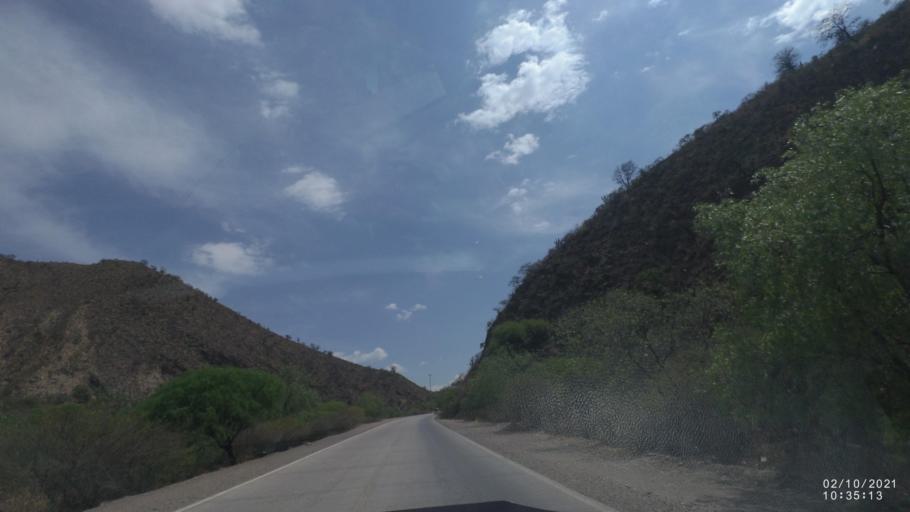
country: BO
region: Cochabamba
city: Capinota
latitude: -17.6641
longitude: -66.2577
